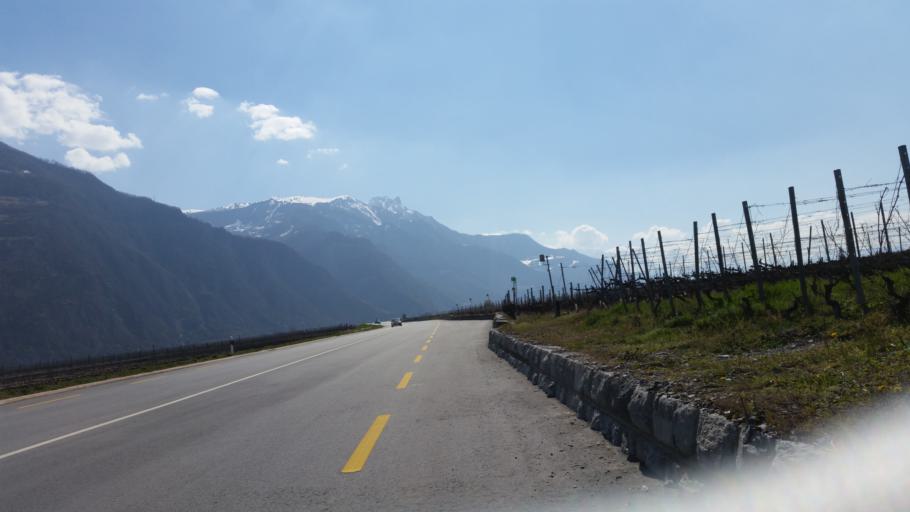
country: CH
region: Valais
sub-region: Conthey District
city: Ardon
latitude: 46.2033
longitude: 7.2491
